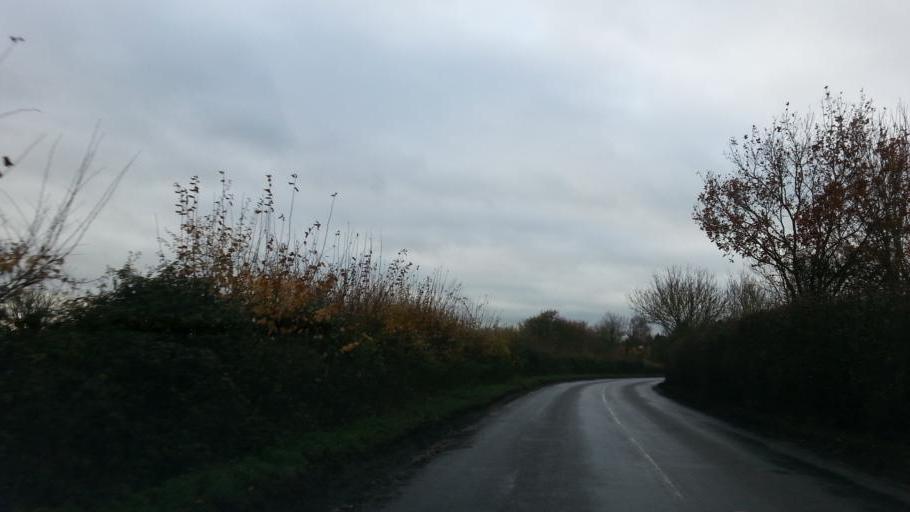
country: GB
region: England
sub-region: Norfolk
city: Harleston
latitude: 52.3134
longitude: 1.3125
